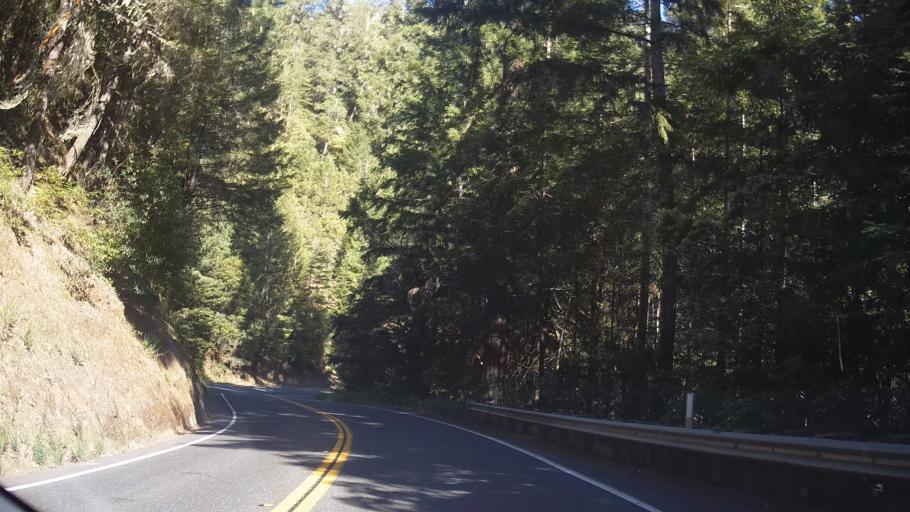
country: US
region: California
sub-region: Mendocino County
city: Brooktrails
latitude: 39.3539
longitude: -123.5102
